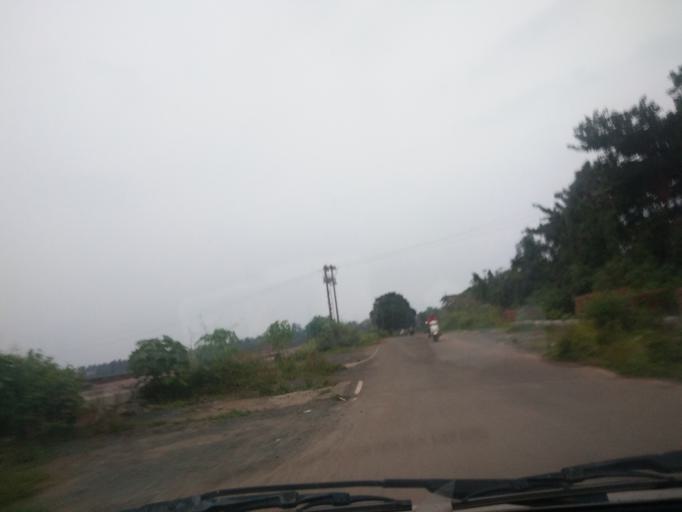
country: IN
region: Goa
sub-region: South Goa
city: Madgaon
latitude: 15.2622
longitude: 73.9559
